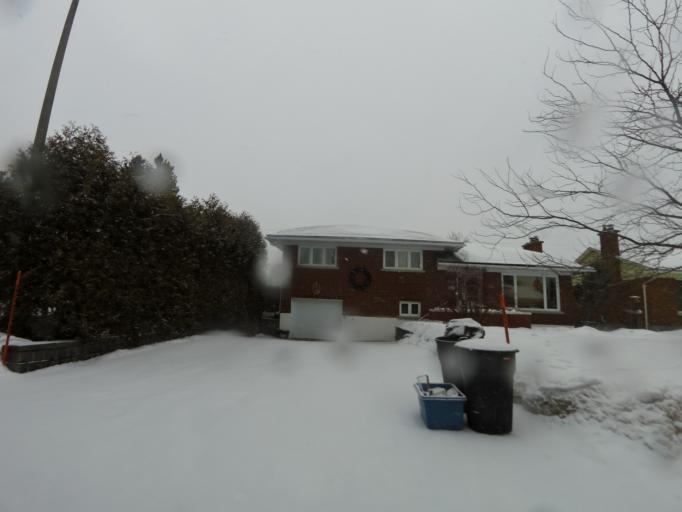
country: CA
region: Ontario
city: Ottawa
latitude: 45.4069
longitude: -75.6373
